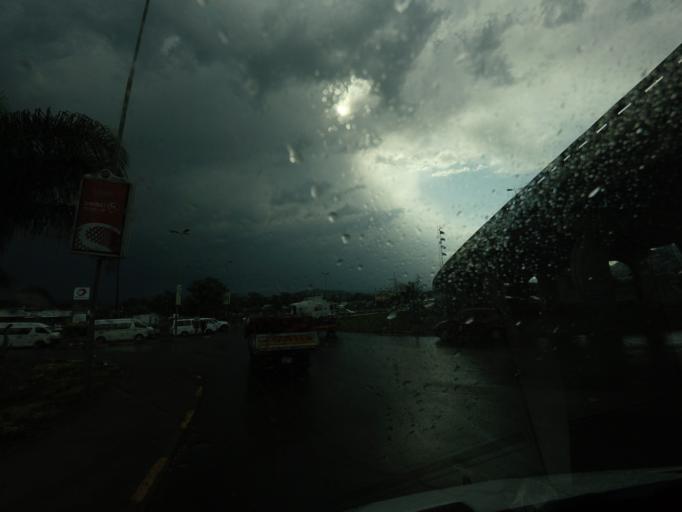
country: SZ
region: Manzini
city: Kwaluseni
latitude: -26.4904
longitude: 31.3037
